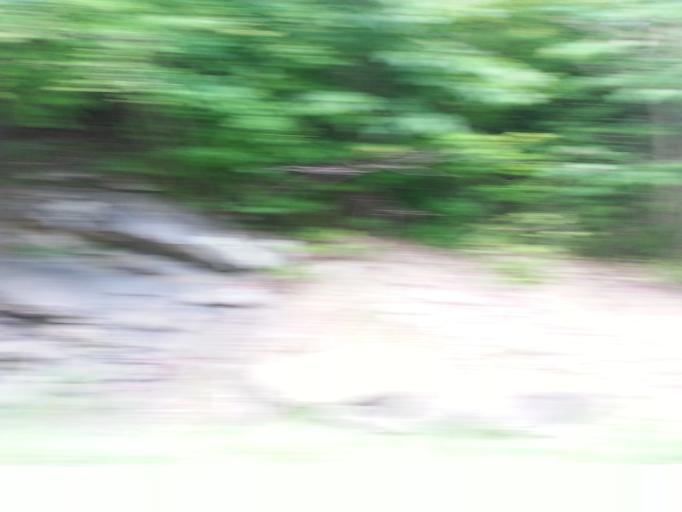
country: US
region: Virginia
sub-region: Lee County
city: Jonesville
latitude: 36.7619
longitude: -83.1402
